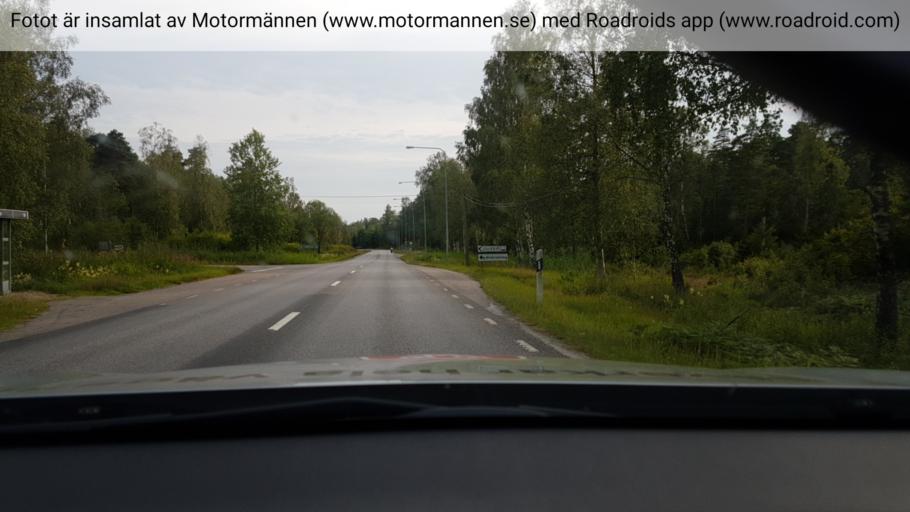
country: SE
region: Vaestra Goetaland
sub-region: Uddevalla Kommun
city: Uddevalla
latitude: 58.3697
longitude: 11.9714
